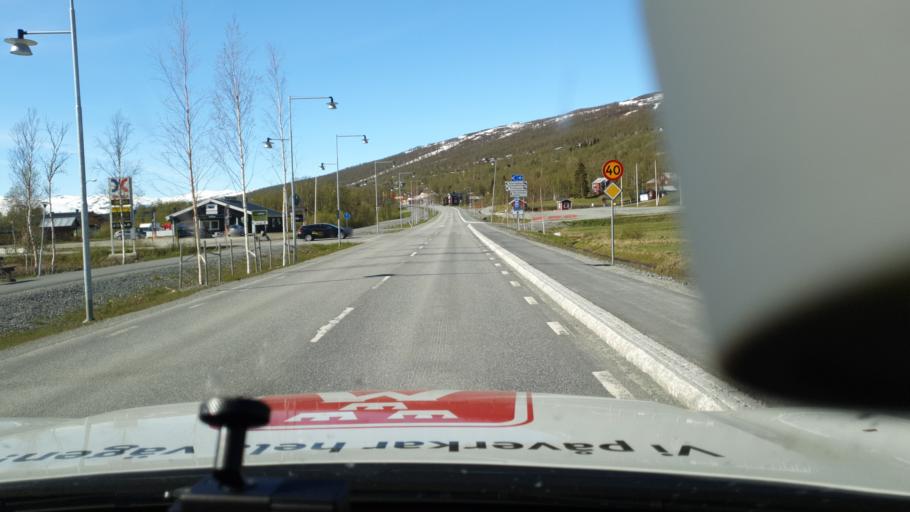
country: NO
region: Nordland
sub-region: Rana
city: Mo i Rana
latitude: 65.8141
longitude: 15.0879
